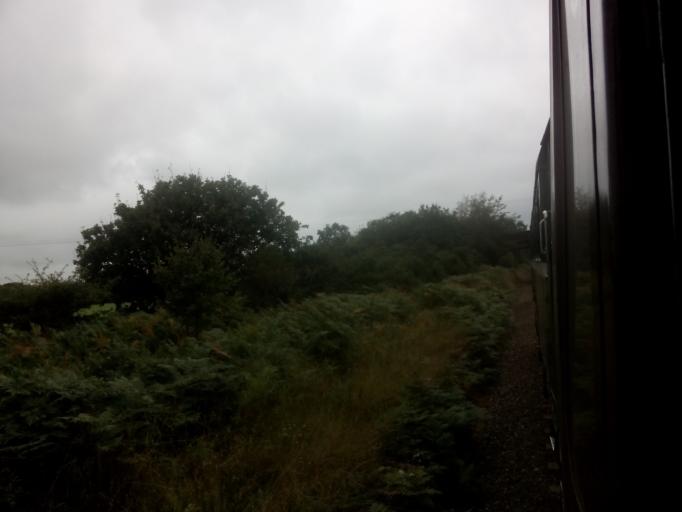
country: GB
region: England
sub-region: Norfolk
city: Briston
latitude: 52.9205
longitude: 1.1139
